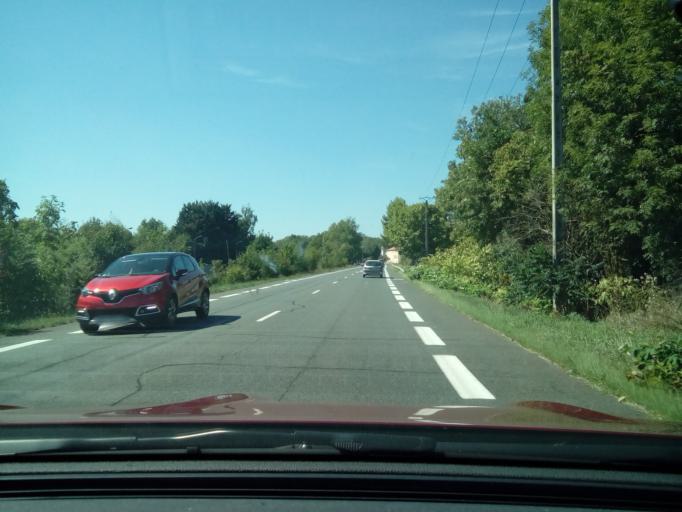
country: FR
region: Rhone-Alpes
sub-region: Departement du Rhone
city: Chatillon
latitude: 45.8874
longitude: 4.6176
